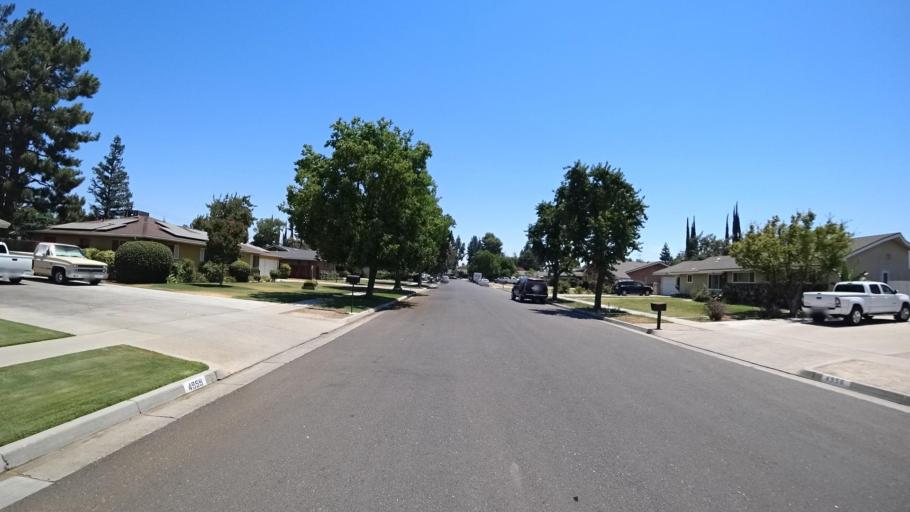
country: US
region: California
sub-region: Fresno County
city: Sunnyside
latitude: 36.7278
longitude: -119.7293
